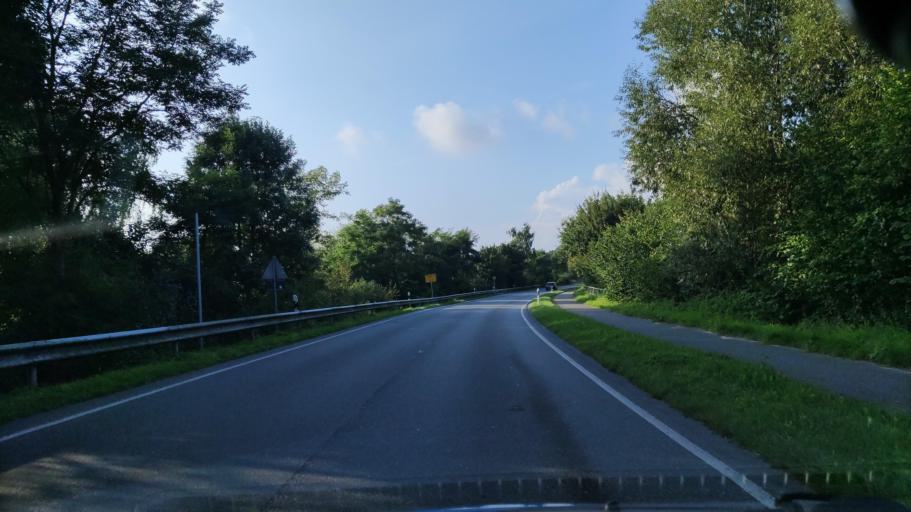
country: DE
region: Schleswig-Holstein
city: Stockelsdorf
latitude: 53.9513
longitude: 10.6219
